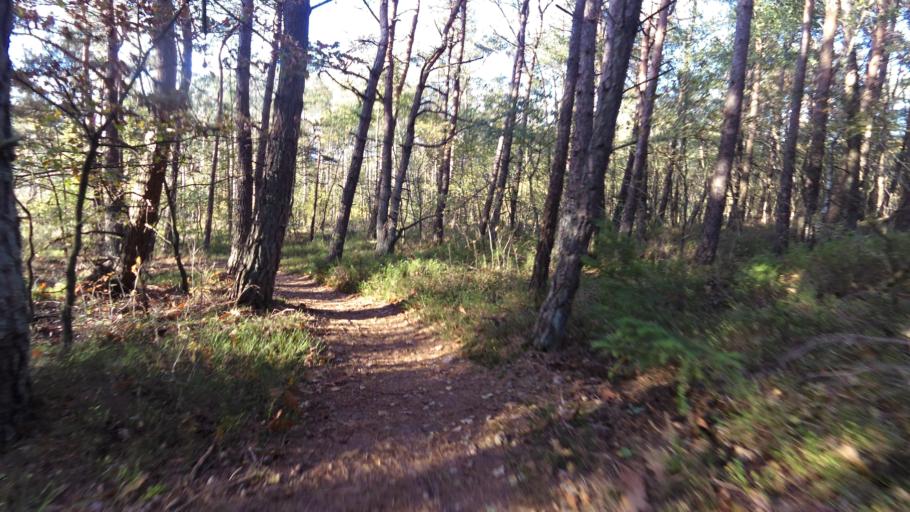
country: NL
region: Gelderland
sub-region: Gemeente Epe
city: Epe
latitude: 52.3932
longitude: 5.9853
